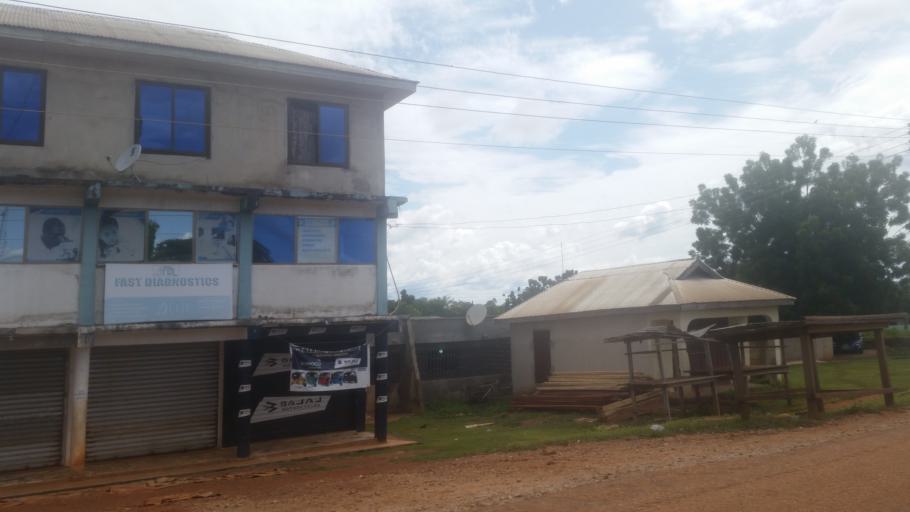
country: GH
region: Western
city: Bibiani
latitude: 6.8048
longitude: -2.5222
